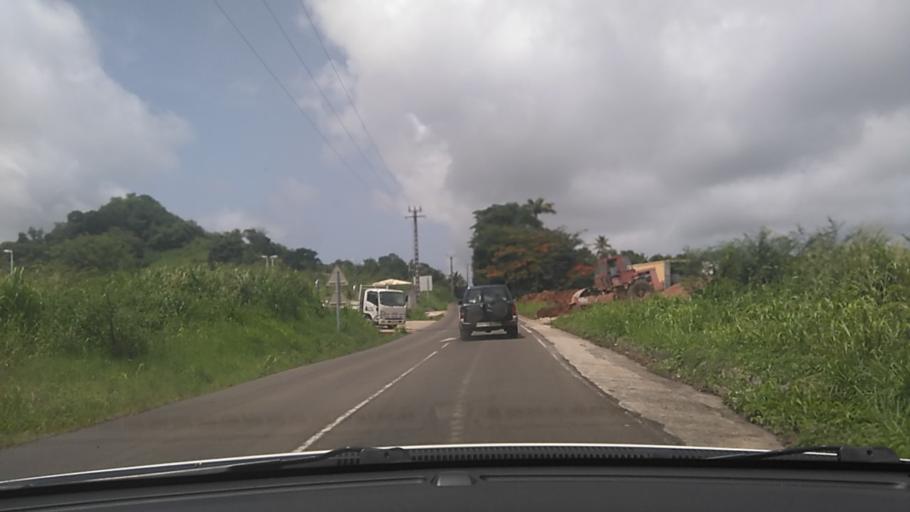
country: MQ
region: Martinique
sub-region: Martinique
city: Saint-Esprit
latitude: 14.5586
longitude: -60.9296
